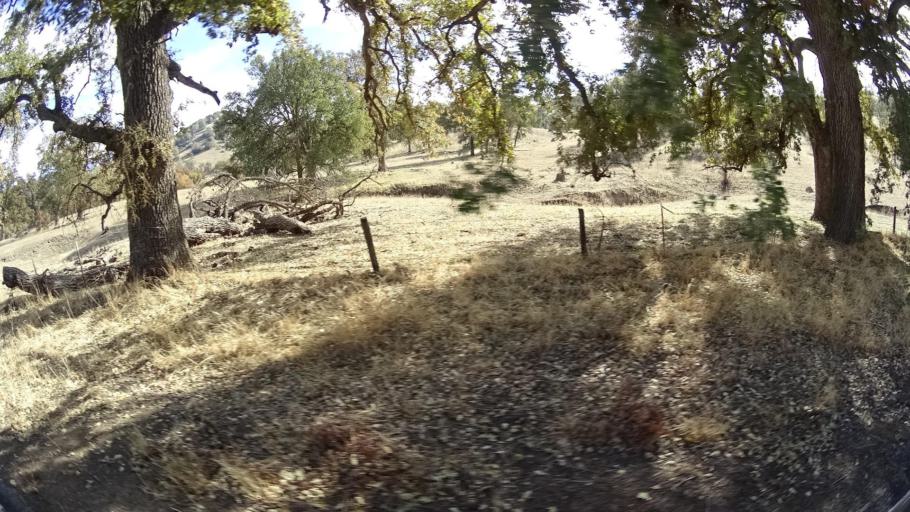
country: US
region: California
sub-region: Kern County
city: Alta Sierra
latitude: 35.6699
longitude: -118.7429
